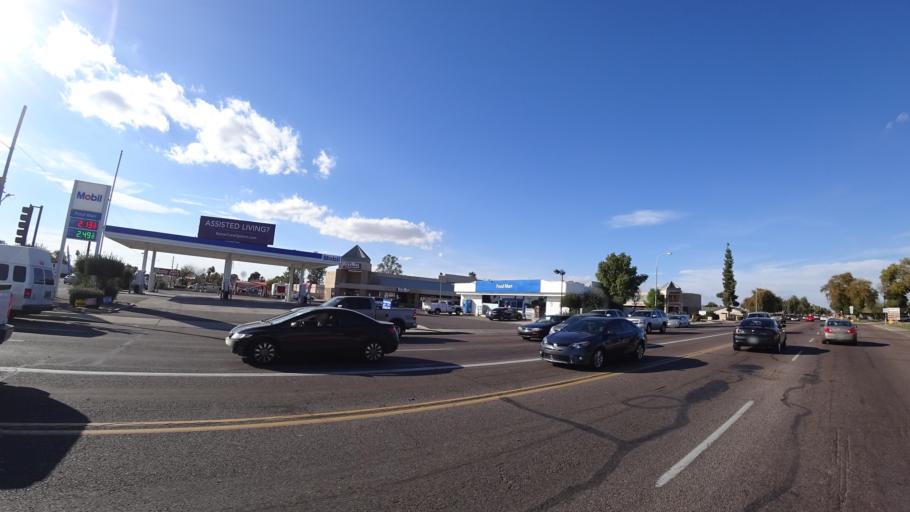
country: US
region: Arizona
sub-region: Maricopa County
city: Tolleson
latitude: 33.4944
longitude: -112.2377
